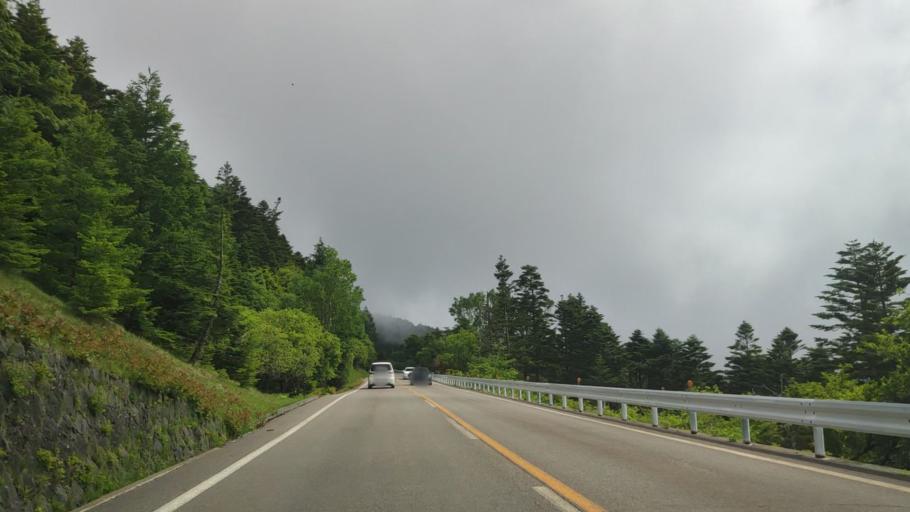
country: JP
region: Yamanashi
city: Fujikawaguchiko
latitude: 35.3984
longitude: 138.6921
